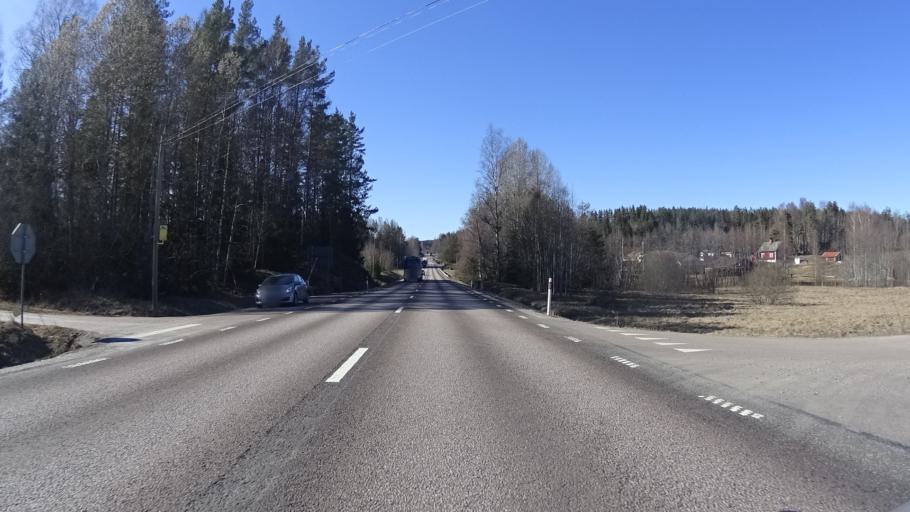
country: SE
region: Vaermland
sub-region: Sunne Kommun
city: Sunne
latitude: 59.6609
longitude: 12.9289
